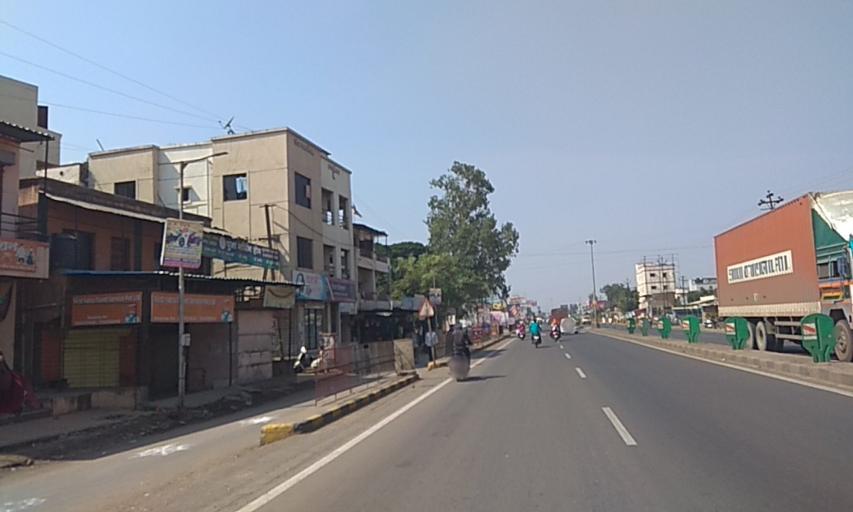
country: IN
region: Maharashtra
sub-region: Pune Division
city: Lohogaon
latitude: 18.4911
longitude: 74.0073
